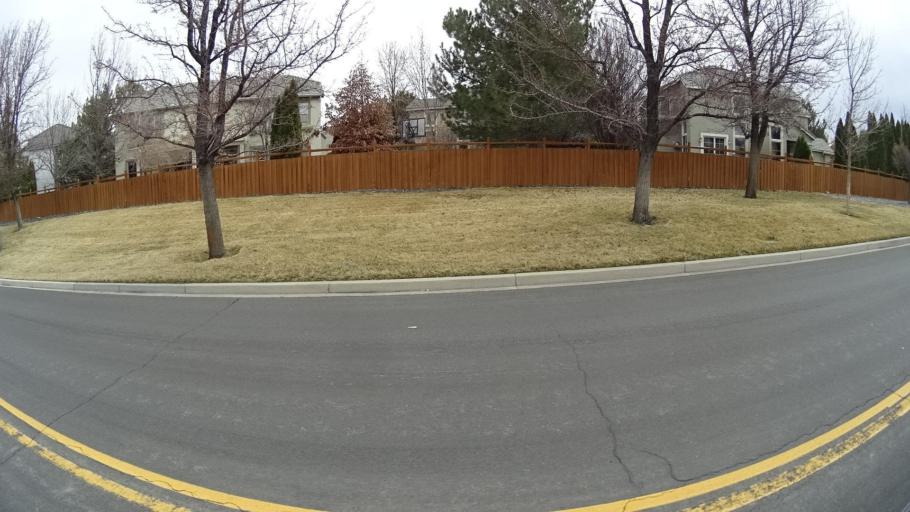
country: US
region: Nevada
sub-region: Washoe County
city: Spanish Springs
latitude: 39.6163
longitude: -119.6817
